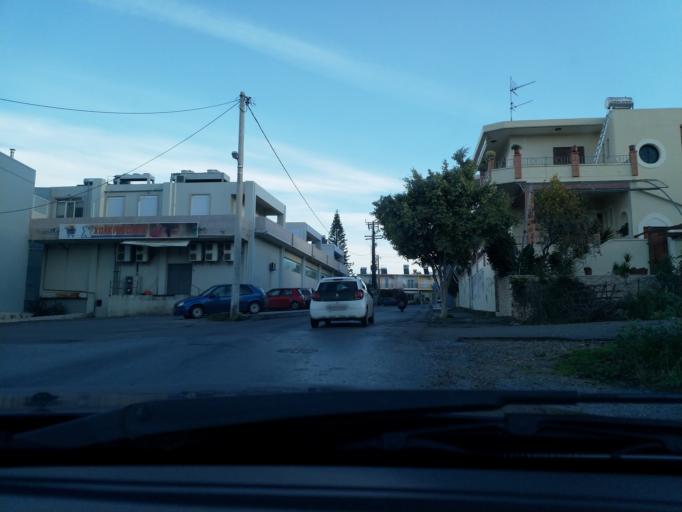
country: GR
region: Crete
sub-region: Nomos Chanias
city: Chania
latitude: 35.5128
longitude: 24.0474
